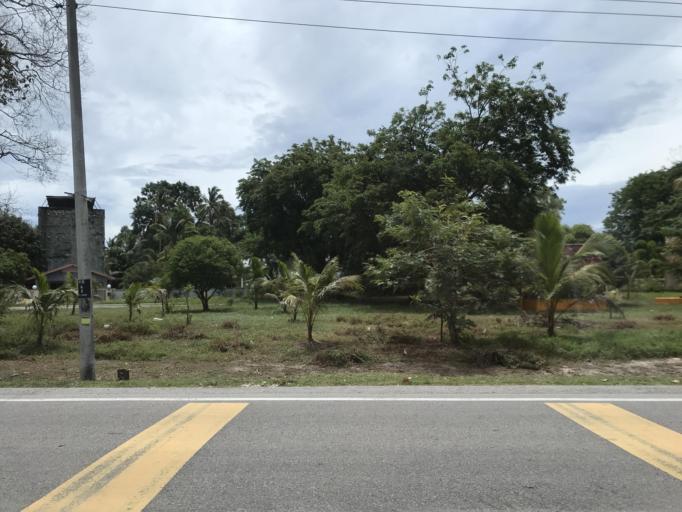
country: MY
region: Kelantan
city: Tumpat
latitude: 6.1755
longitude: 102.1984
